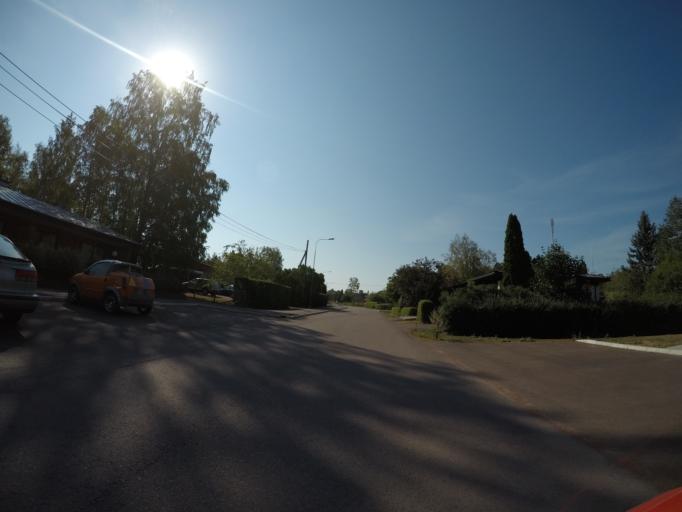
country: AX
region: Alands landsbygd
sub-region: Finstroem
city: Finstroem
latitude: 60.2274
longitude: 19.9789
